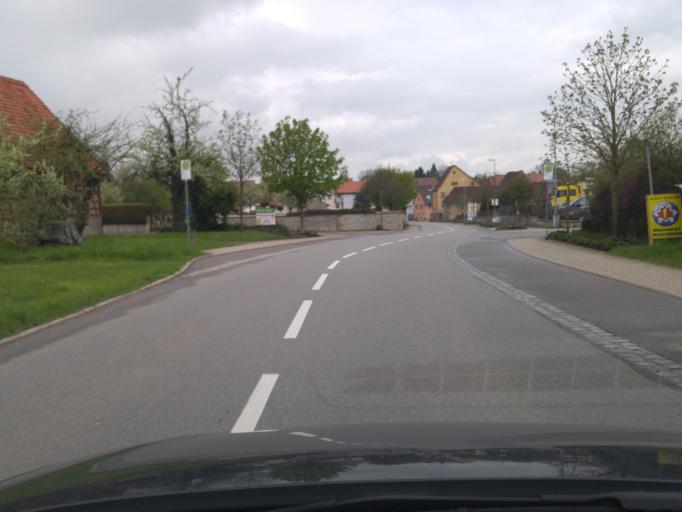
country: DE
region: Baden-Wuerttemberg
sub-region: Karlsruhe Region
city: Huffenhardt
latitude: 49.2884
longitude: 9.0841
